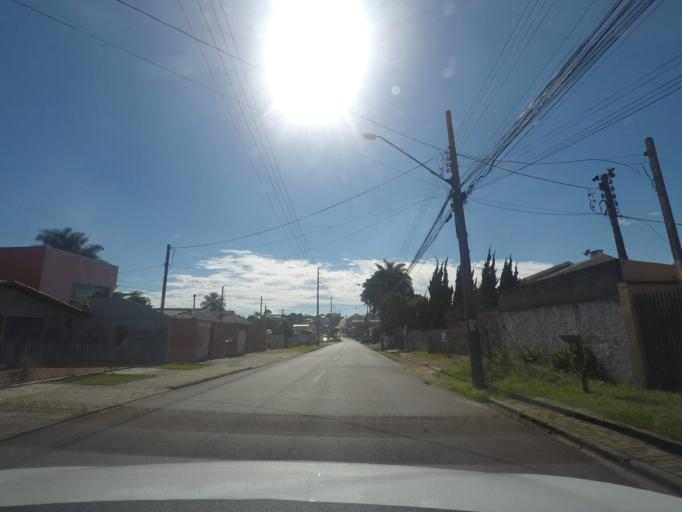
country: BR
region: Parana
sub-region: Sao Jose Dos Pinhais
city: Sao Jose dos Pinhais
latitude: -25.5074
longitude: -49.2797
